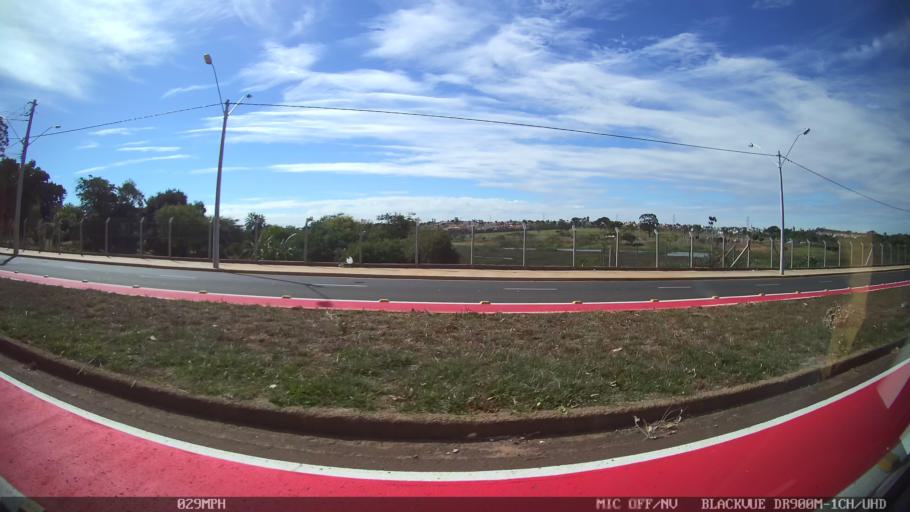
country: BR
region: Sao Paulo
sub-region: Sao Jose Do Rio Preto
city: Sao Jose do Rio Preto
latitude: -20.8260
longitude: -49.3467
